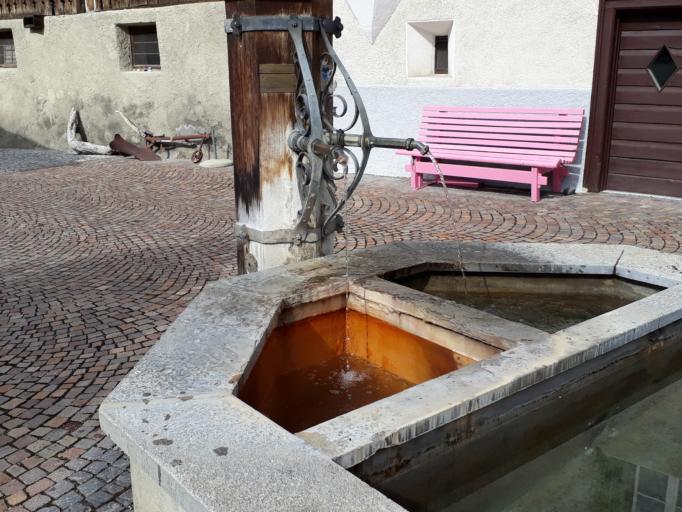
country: CH
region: Grisons
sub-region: Inn District
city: Scuol
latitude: 46.7981
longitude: 10.3026
